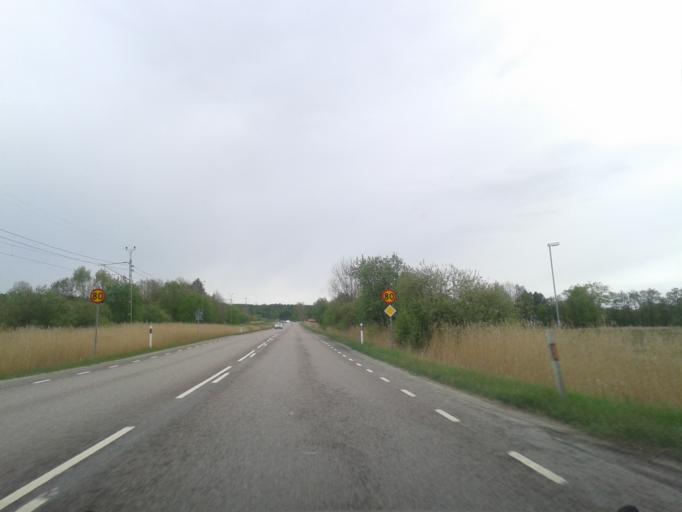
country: SE
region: Vaestra Goetaland
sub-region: Stenungsunds Kommun
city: Stora Hoga
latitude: 58.0071
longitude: 11.8297
